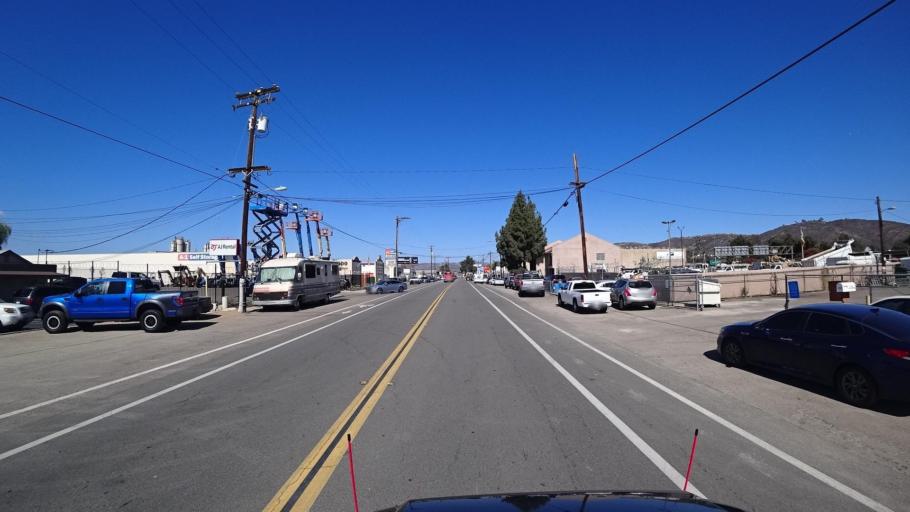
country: US
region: California
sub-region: San Diego County
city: El Cajon
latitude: 32.8149
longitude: -116.9623
